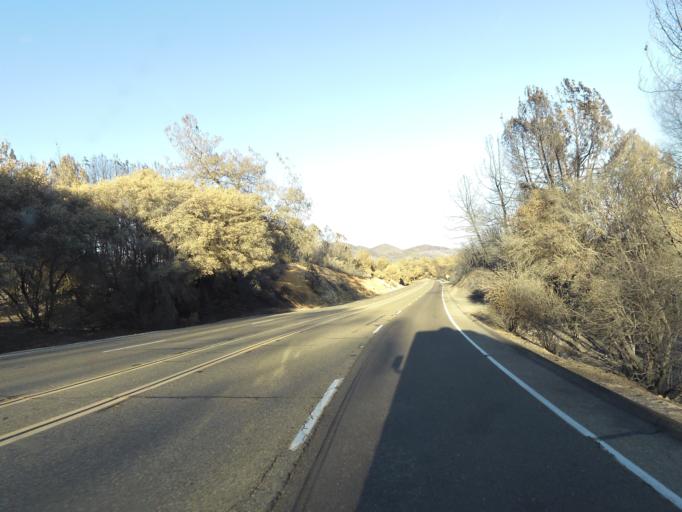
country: US
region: California
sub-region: Mariposa County
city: Mariposa
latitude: 37.4765
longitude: -120.0474
